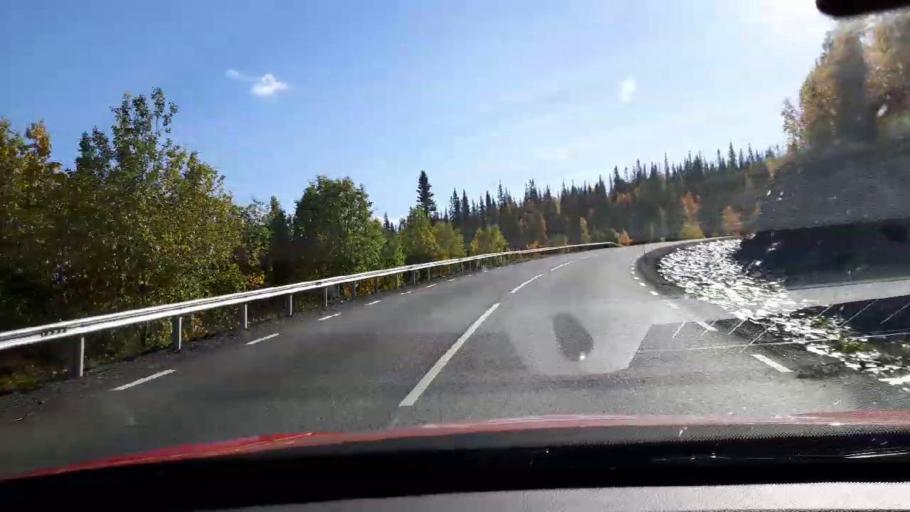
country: NO
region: Nord-Trondelag
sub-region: Royrvik
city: Royrvik
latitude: 64.8504
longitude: 14.1779
